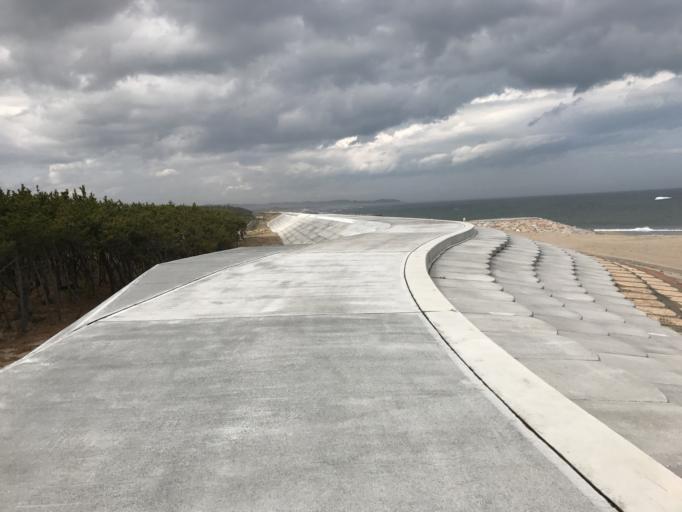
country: JP
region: Fukushima
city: Iwaki
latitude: 37.0445
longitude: 140.9728
